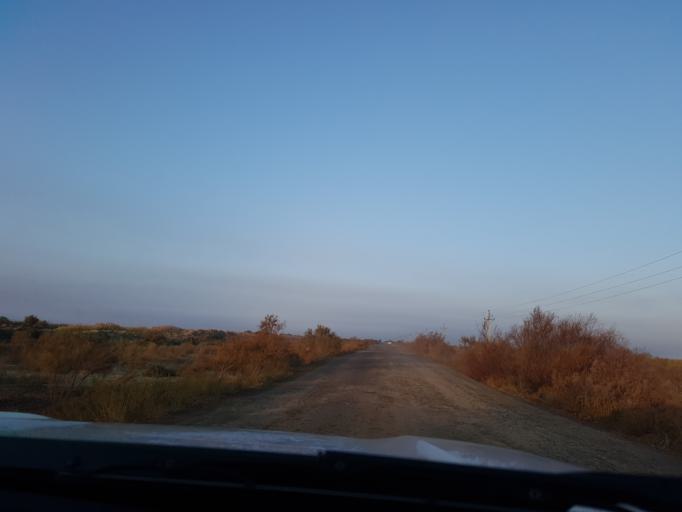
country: TM
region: Dasoguz
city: Koeneuergench
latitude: 41.8444
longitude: 58.5845
